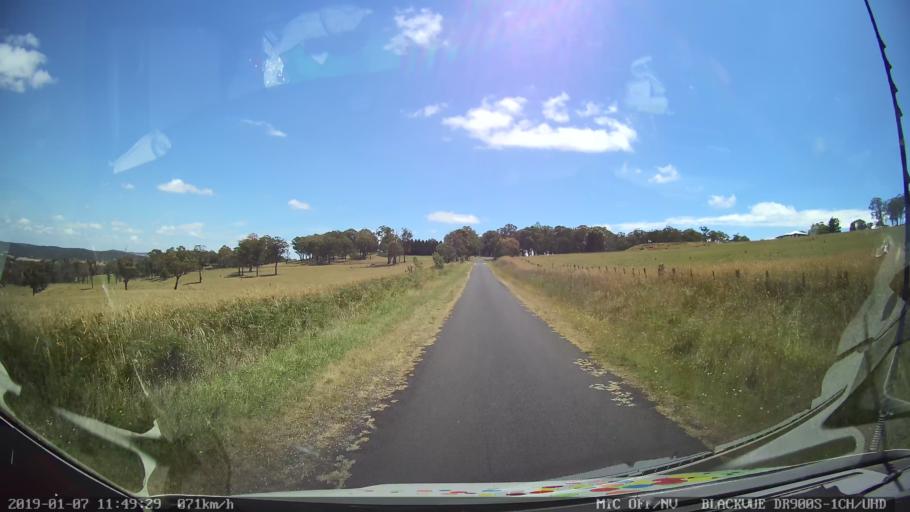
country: AU
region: New South Wales
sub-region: Guyra
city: Guyra
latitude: -30.3185
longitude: 151.6289
